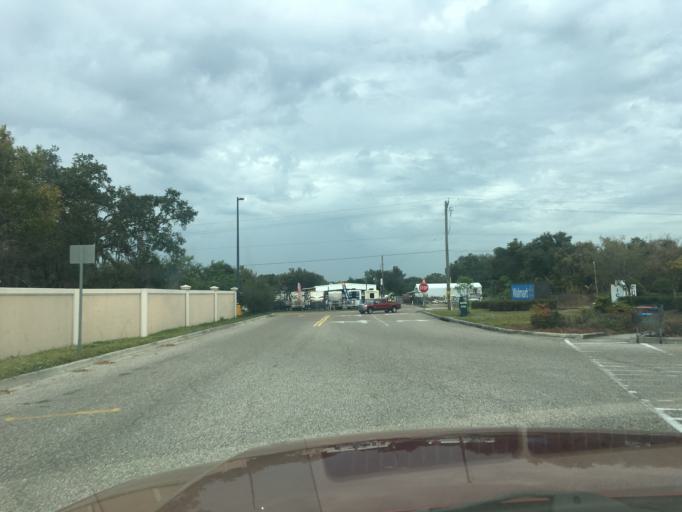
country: US
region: Florida
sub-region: Hillsborough County
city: Gibsonton
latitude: 27.8489
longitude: -82.3556
